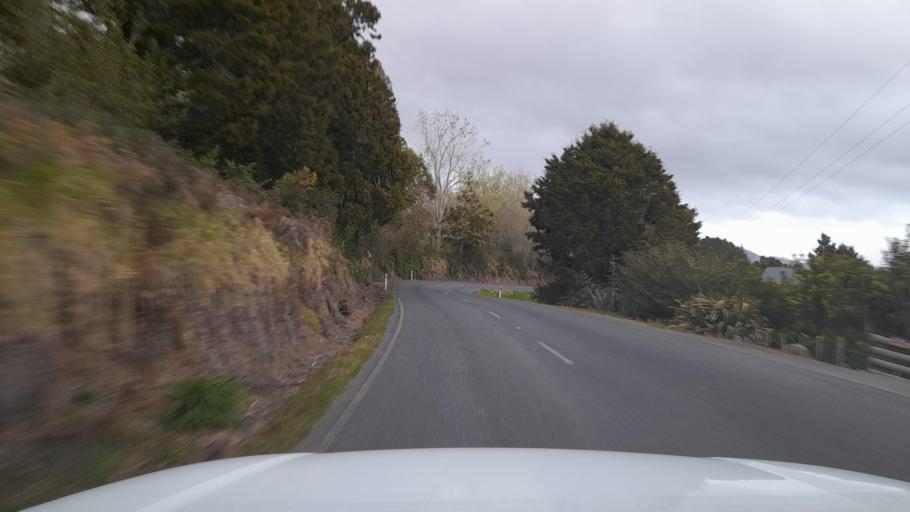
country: NZ
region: Northland
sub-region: Whangarei
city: Maungatapere
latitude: -35.6390
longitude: 174.2145
